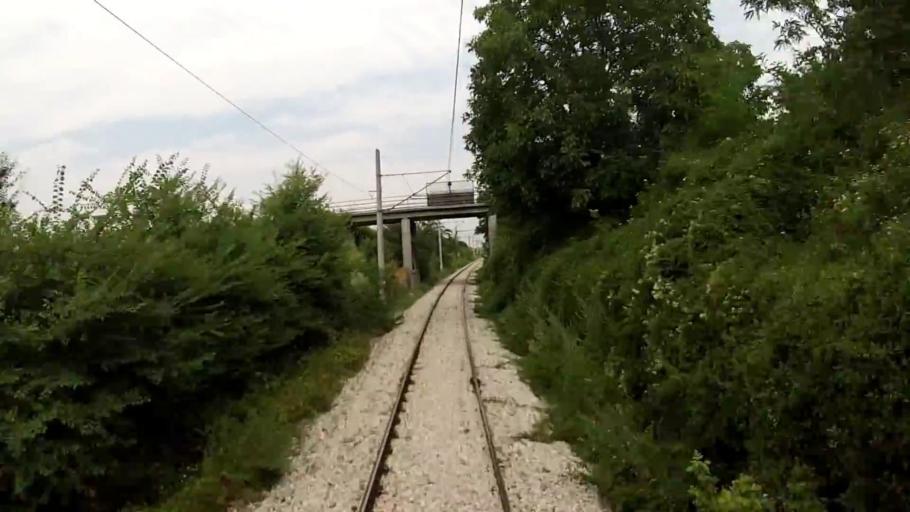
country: BG
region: Blagoevgrad
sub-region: Obshtina Blagoevgrad
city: Blagoevgrad
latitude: 41.9782
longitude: 23.0897
